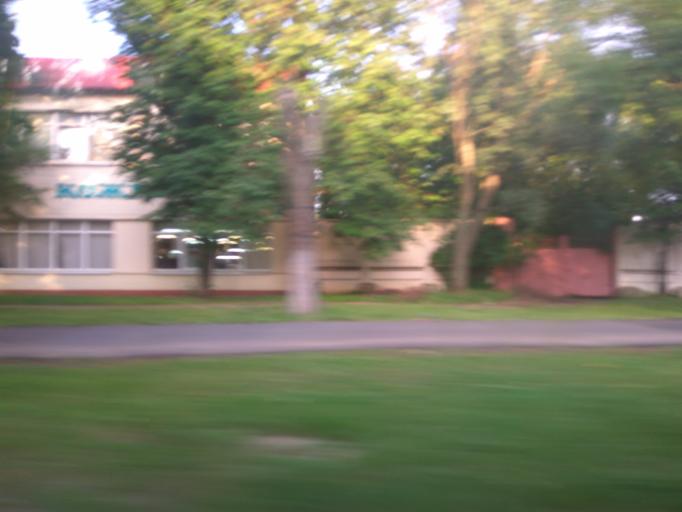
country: RU
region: Moskovskaya
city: Biryulevo Zapadnoye
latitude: 55.5993
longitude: 37.6210
